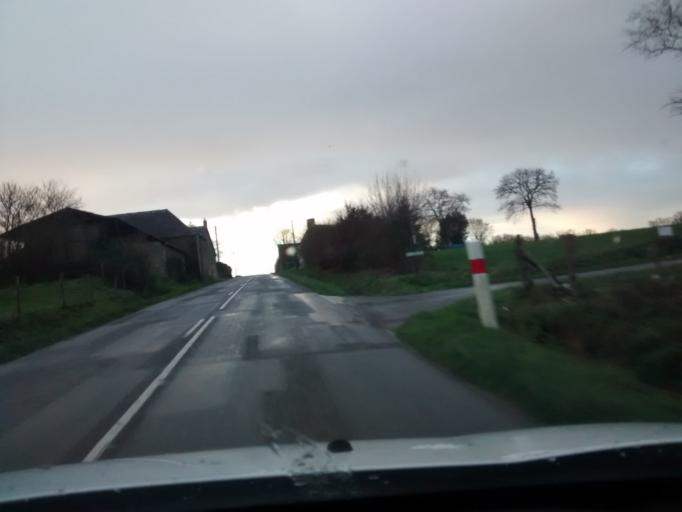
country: FR
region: Brittany
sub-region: Departement d'Ille-et-Vilaine
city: Bais
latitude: 47.9912
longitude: -1.2864
